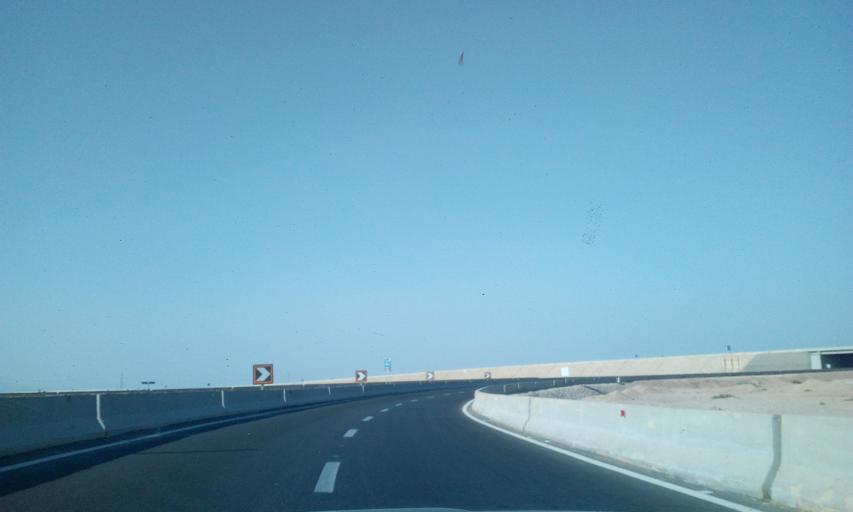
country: EG
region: As Suways
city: Ain Sukhna
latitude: 29.1075
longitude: 32.5302
